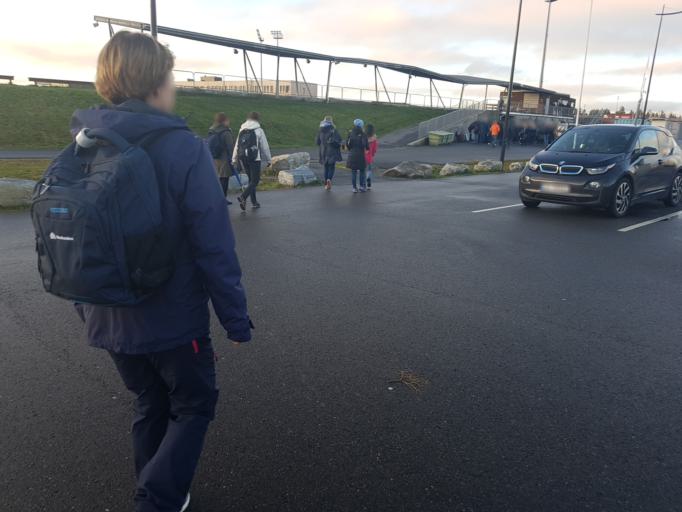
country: NO
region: Akershus
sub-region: Ullensaker
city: Jessheim
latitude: 60.1492
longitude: 11.1934
